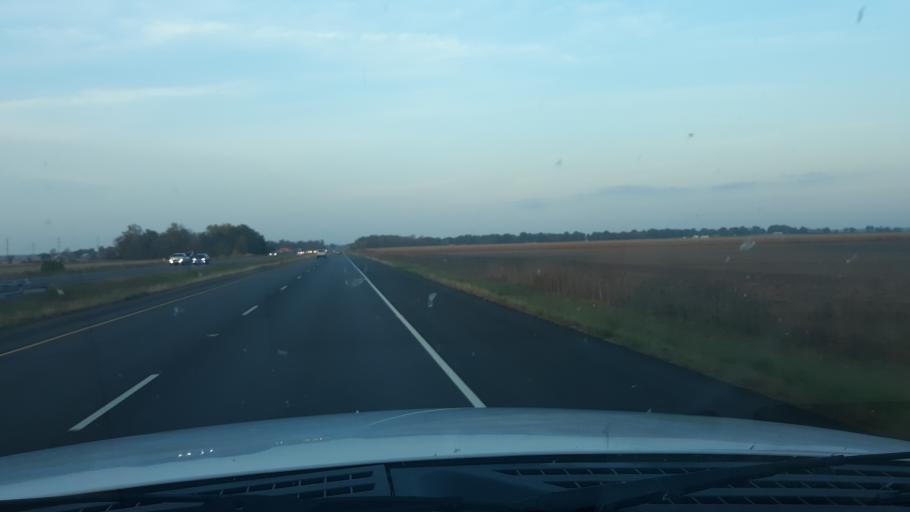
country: US
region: Illinois
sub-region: Saline County
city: Harrisburg
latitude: 37.7754
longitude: -88.5024
